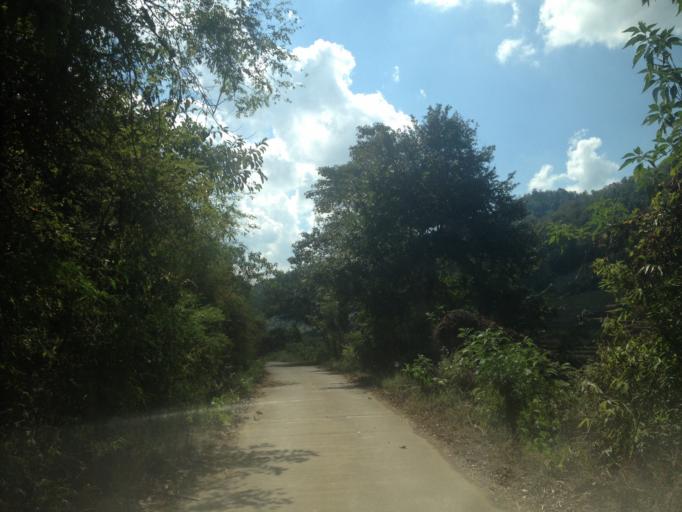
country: TH
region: Mae Hong Son
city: Ban Huai I Huak
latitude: 18.1001
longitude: 98.1889
